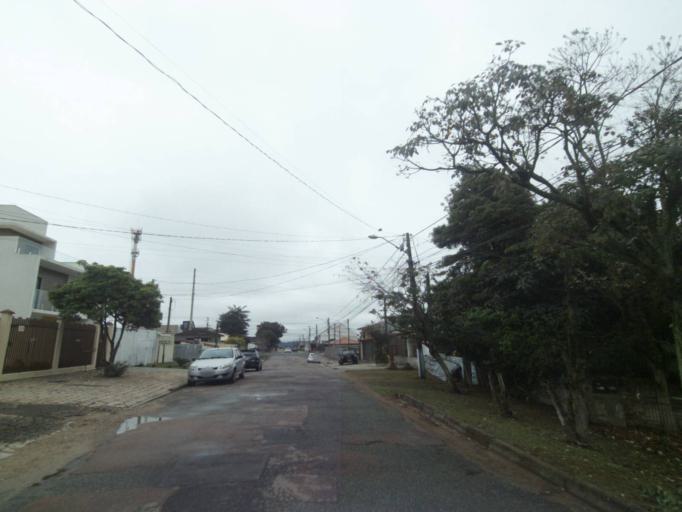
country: BR
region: Parana
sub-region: Curitiba
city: Curitiba
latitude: -25.5170
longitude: -49.3034
